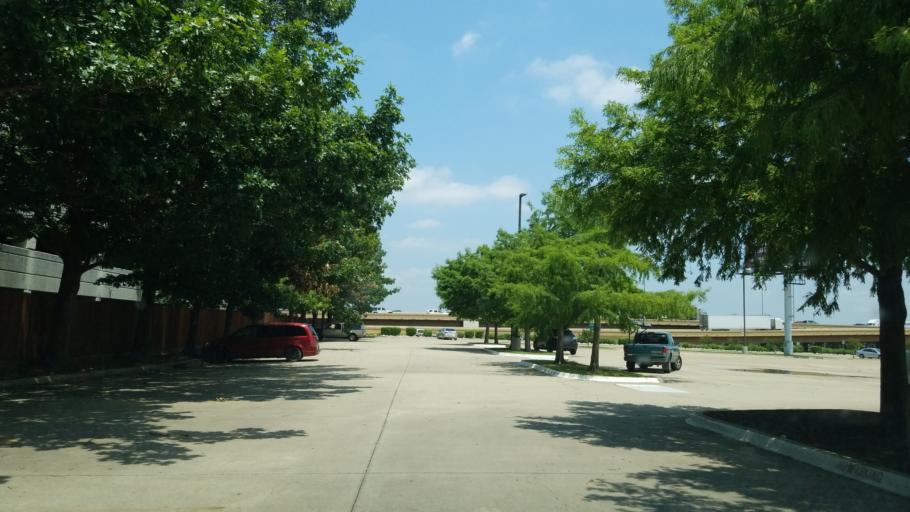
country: US
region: Texas
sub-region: Dallas County
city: Farmers Branch
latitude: 32.9110
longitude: -96.8754
